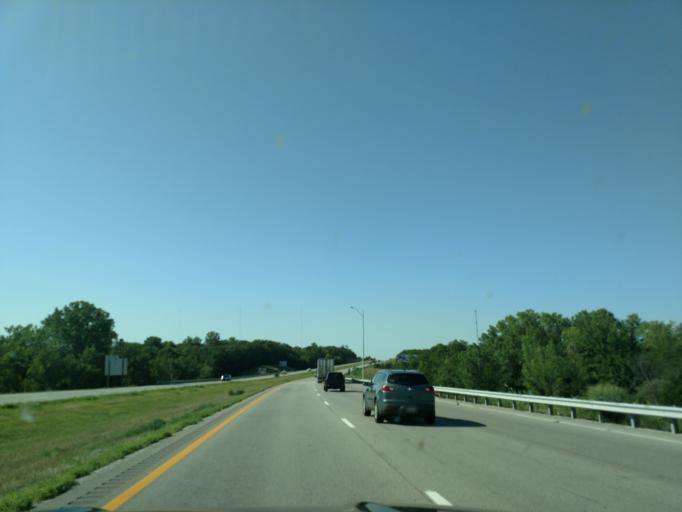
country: US
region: Missouri
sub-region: Andrew County
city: Country Club Village
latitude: 39.8188
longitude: -94.8048
